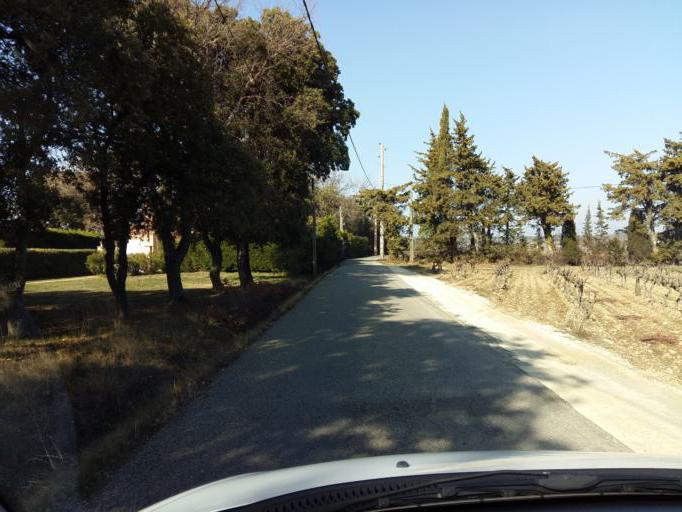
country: FR
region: Provence-Alpes-Cote d'Azur
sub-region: Departement du Vaucluse
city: Valreas
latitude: 44.3811
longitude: 4.9628
